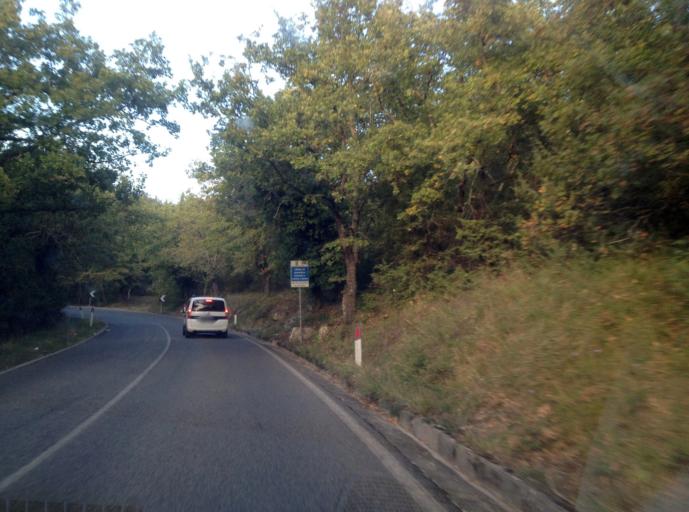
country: IT
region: Tuscany
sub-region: Provincia di Siena
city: Castellina in Chianti
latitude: 43.4275
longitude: 11.3063
